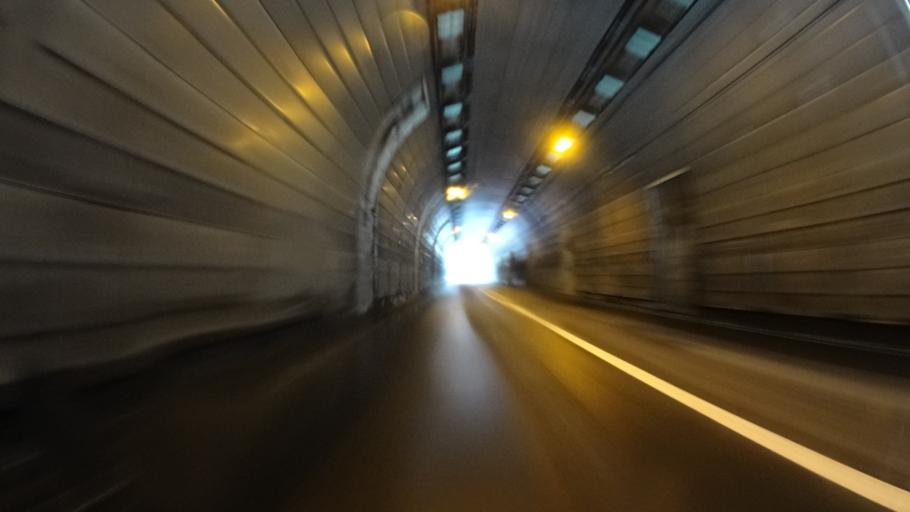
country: JP
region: Yamanashi
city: Uenohara
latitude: 35.7813
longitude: 139.0241
